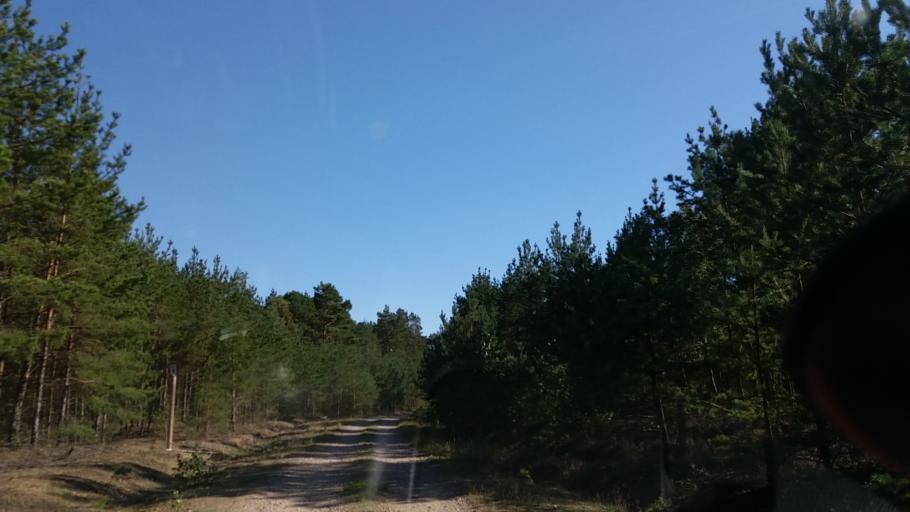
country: PL
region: West Pomeranian Voivodeship
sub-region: Powiat szczecinecki
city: Borne Sulinowo
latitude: 53.5597
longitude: 16.5044
